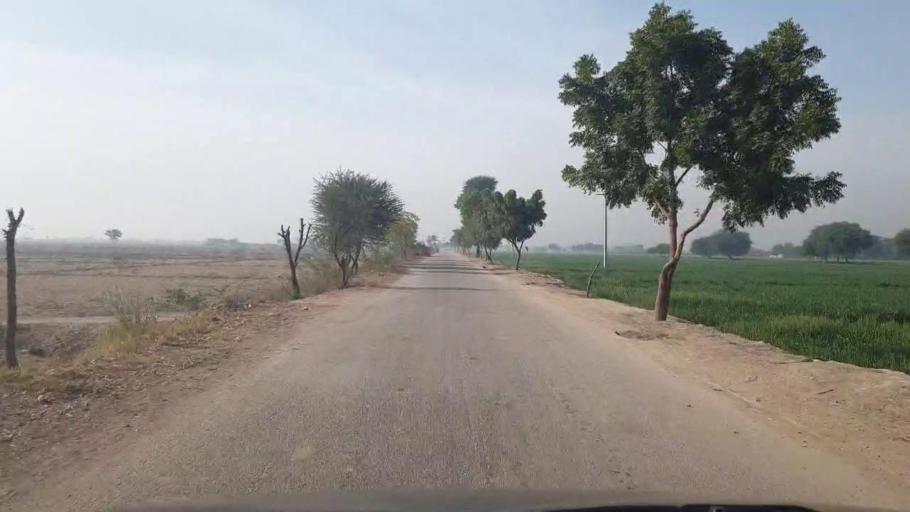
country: PK
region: Sindh
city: Umarkot
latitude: 25.3535
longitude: 69.6991
